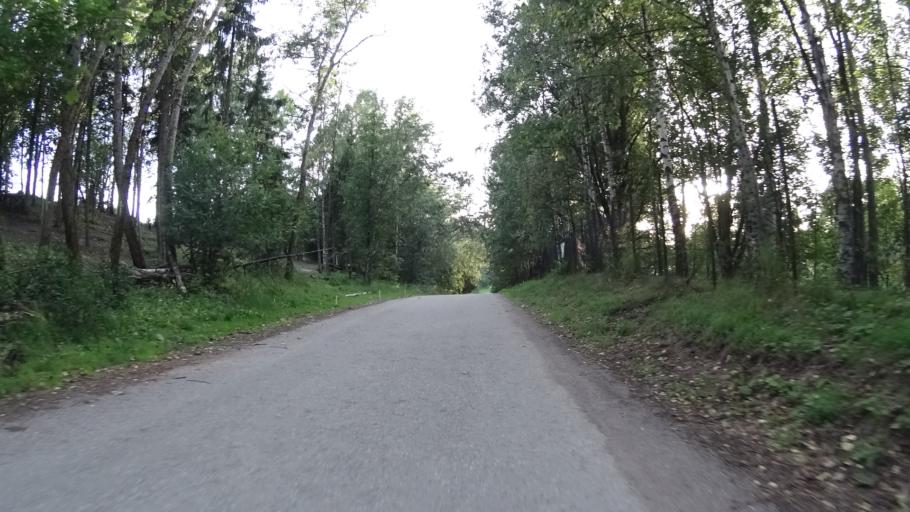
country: FI
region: Uusimaa
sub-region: Helsinki
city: Teekkarikylae
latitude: 60.2138
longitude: 24.8427
